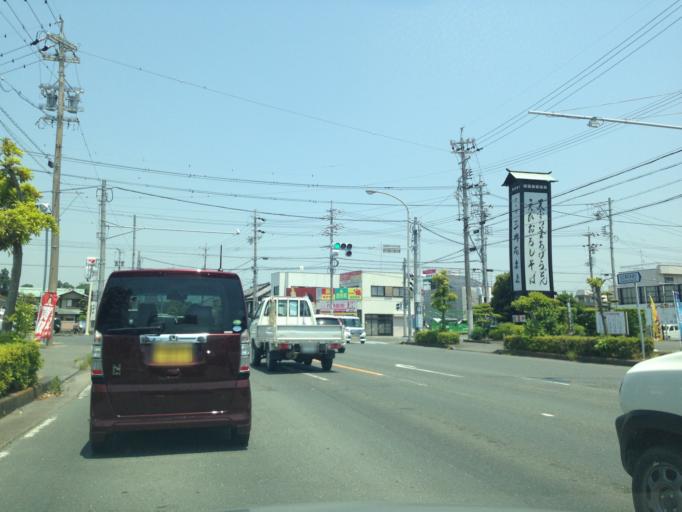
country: JP
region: Shizuoka
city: Iwata
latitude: 34.7242
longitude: 137.8581
